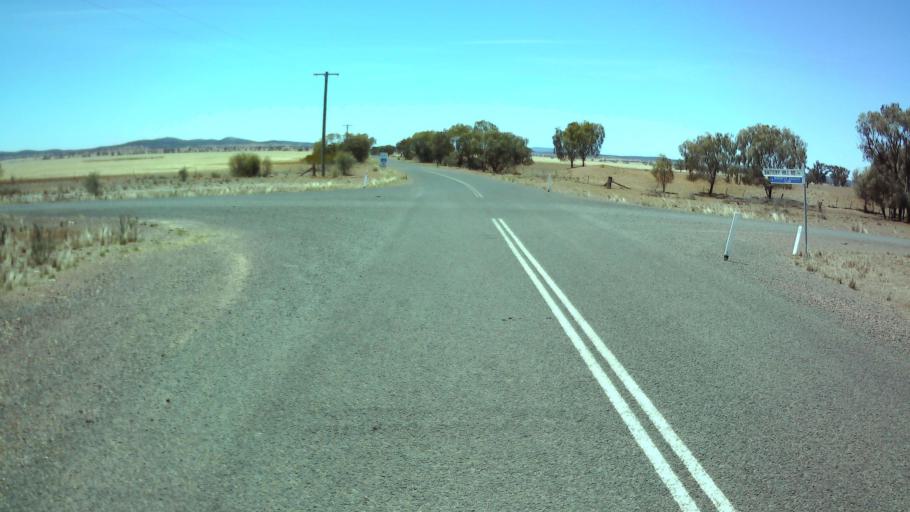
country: AU
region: New South Wales
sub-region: Forbes
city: Forbes
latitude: -33.6742
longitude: 147.6744
